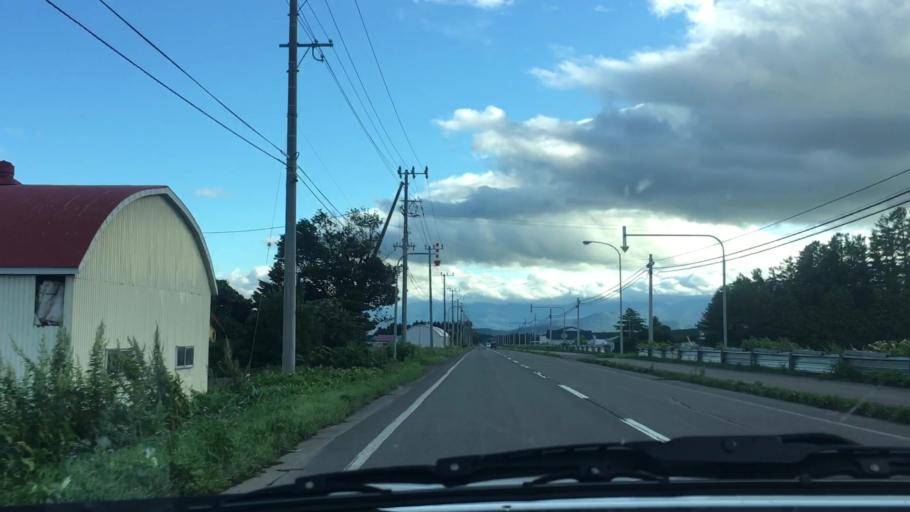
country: JP
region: Hokkaido
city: Otofuke
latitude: 43.1493
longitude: 142.8995
